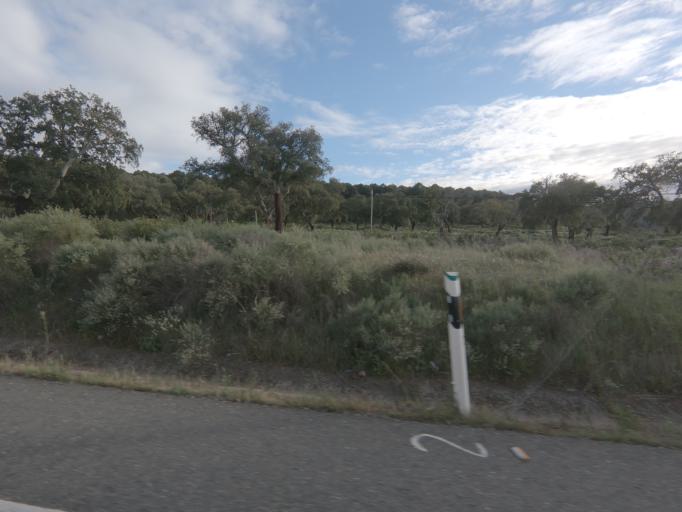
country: ES
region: Extremadura
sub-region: Provincia de Caceres
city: Casas de Millan
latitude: 39.8213
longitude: -6.3671
